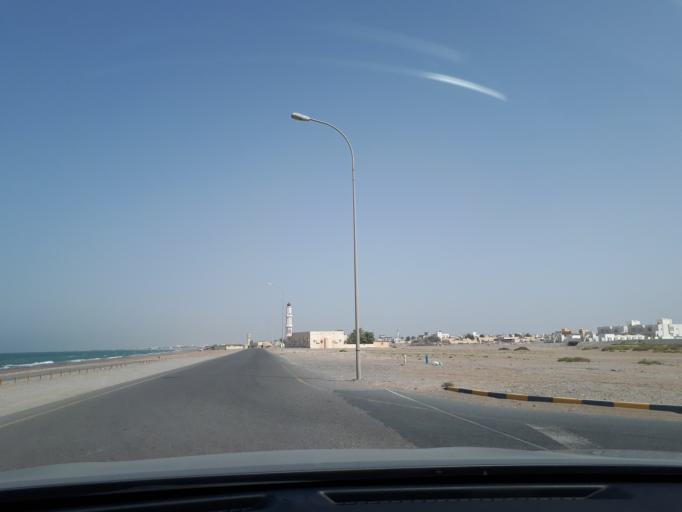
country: OM
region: Al Batinah
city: Barka'
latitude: 23.7224
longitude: 57.8516
